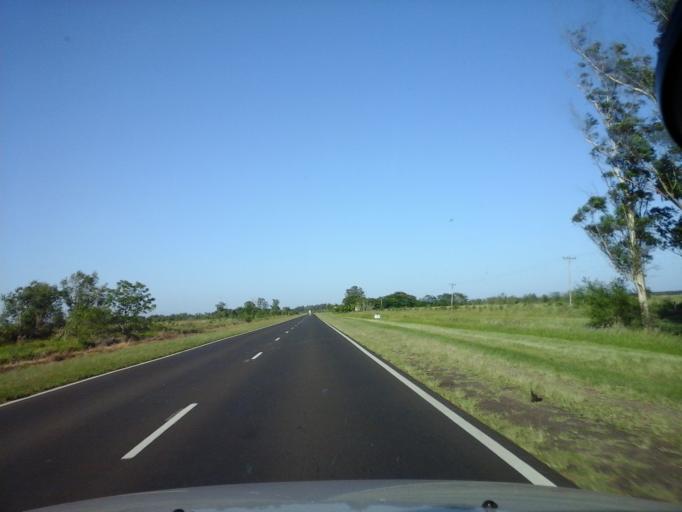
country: AR
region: Corrientes
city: Ita Ibate
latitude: -27.4437
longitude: -57.3770
